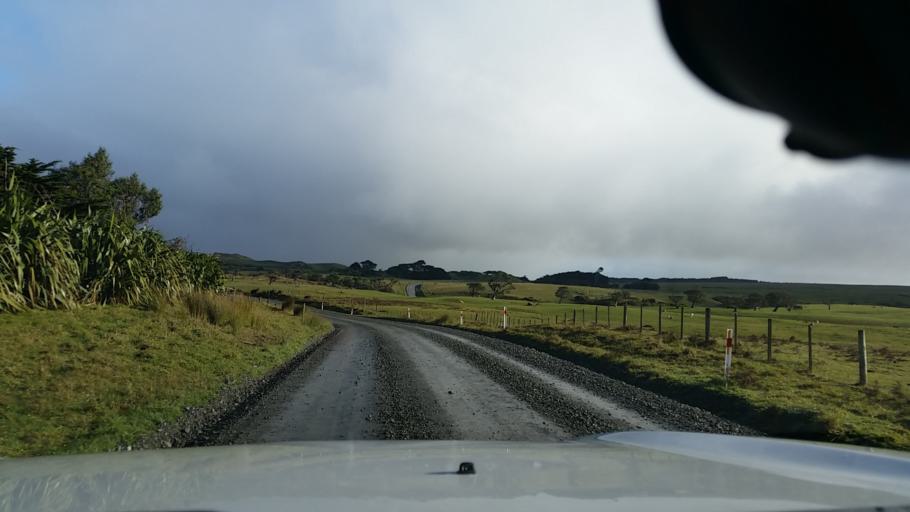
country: NZ
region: Chatham Islands
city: Waitangi
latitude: -43.8201
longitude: -176.5735
